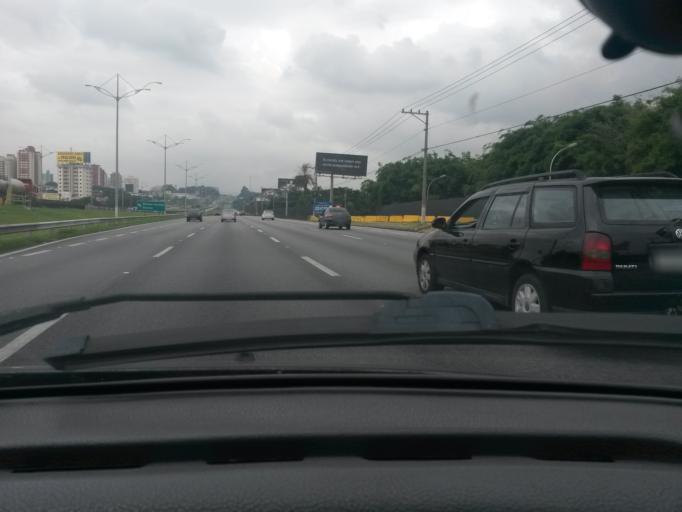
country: BR
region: Sao Paulo
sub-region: Sao Bernardo Do Campo
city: Sao Bernardo do Campo
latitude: -23.6591
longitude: -46.5767
